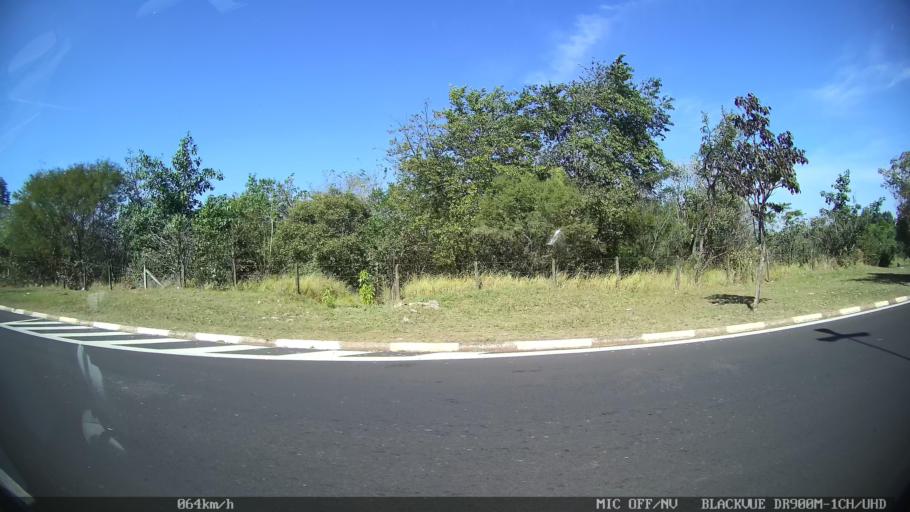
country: BR
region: Sao Paulo
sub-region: Franca
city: Franca
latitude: -20.5554
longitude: -47.4392
